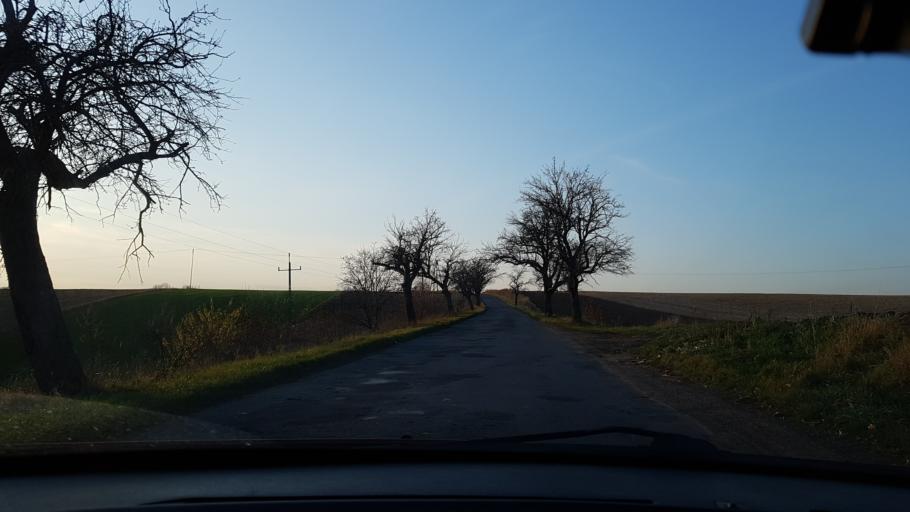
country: PL
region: Lower Silesian Voivodeship
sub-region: Powiat zabkowicki
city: Henrykow
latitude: 50.6583
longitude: 17.0096
